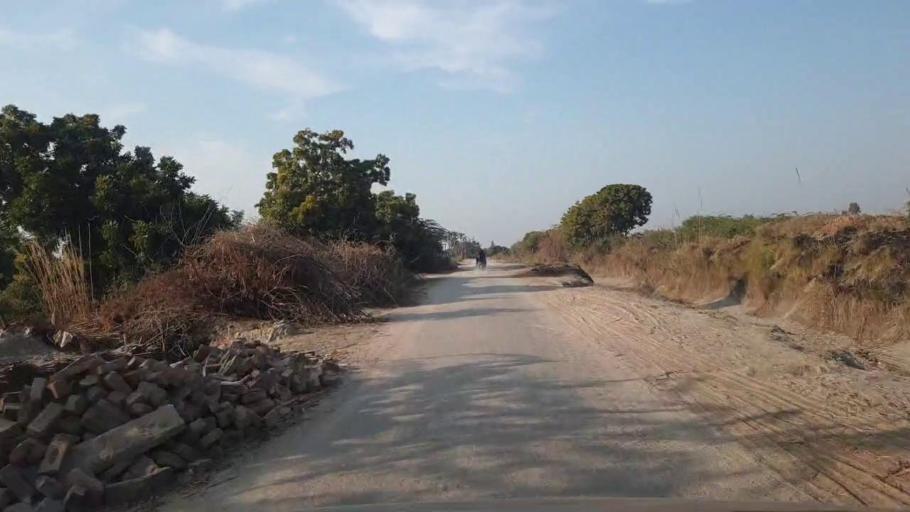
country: PK
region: Sindh
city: Shahpur Chakar
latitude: 26.1526
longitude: 68.6418
